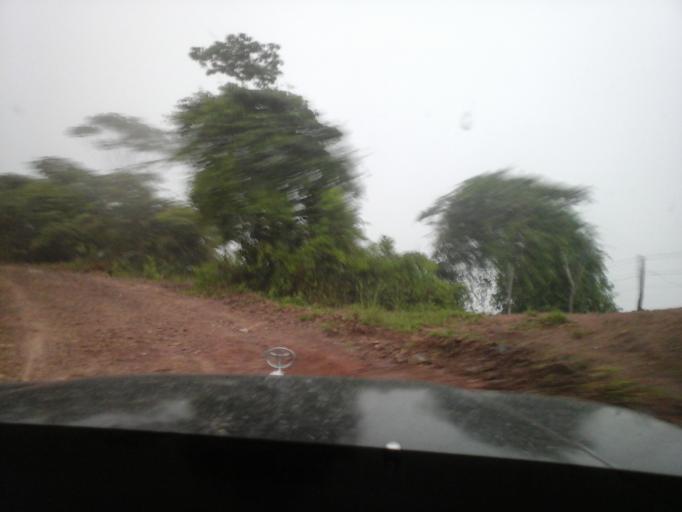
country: CO
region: Cesar
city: Agustin Codazzi
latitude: 9.9385
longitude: -73.1417
